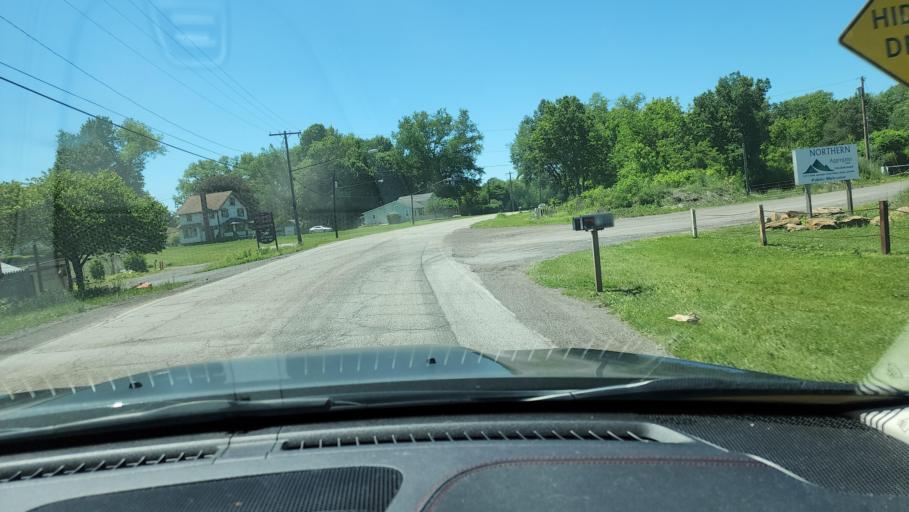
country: US
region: Ohio
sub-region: Trumbull County
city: Mineral Ridge
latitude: 41.1595
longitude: -80.7722
